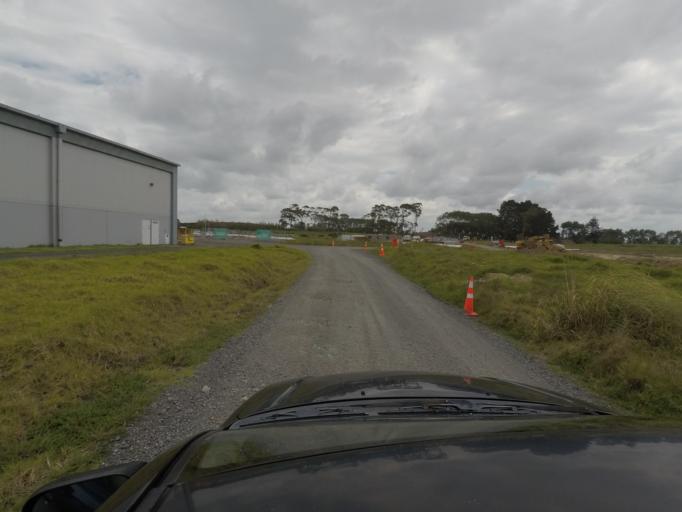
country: NZ
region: Auckland
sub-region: Auckland
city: Mangere
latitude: -36.9965
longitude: 174.7894
